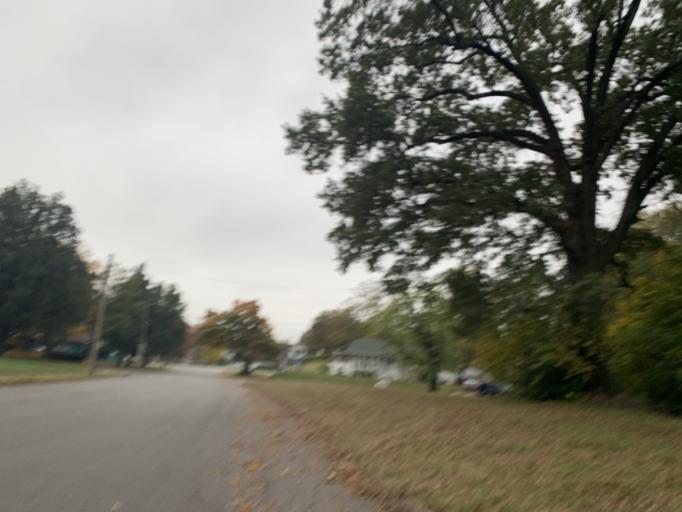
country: US
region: Indiana
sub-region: Floyd County
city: New Albany
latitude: 38.2510
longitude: -85.8060
